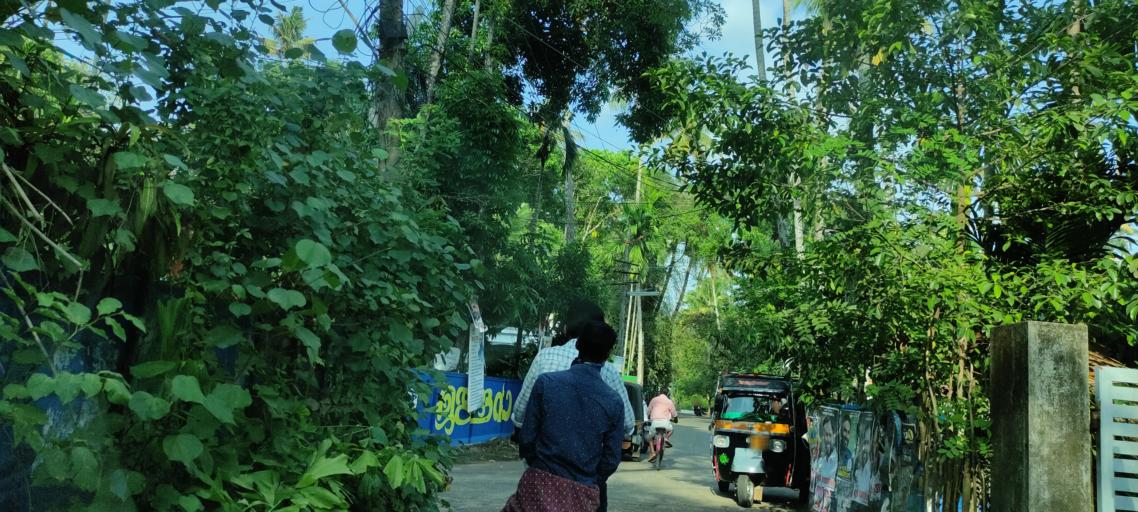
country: IN
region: Kerala
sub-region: Alappuzha
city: Vayalar
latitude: 9.7276
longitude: 76.2904
